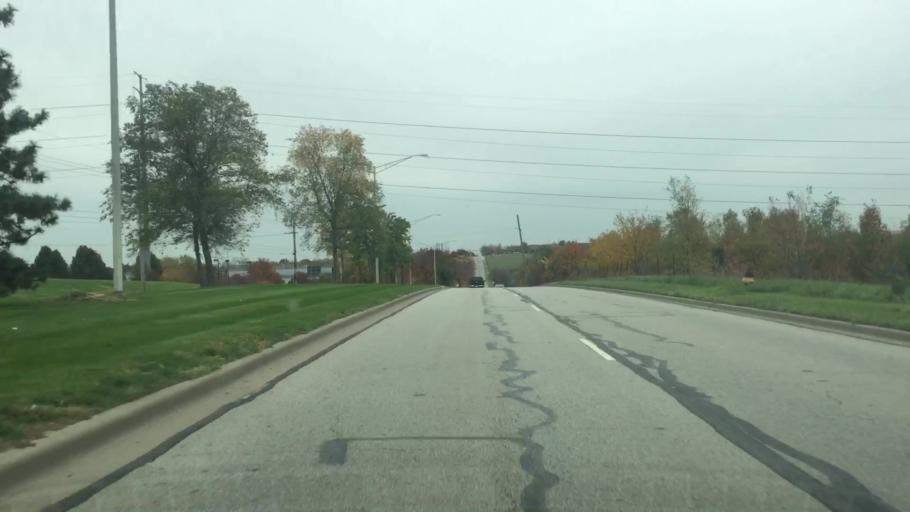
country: US
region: Kansas
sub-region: Johnson County
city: Lenexa
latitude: 38.9359
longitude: -94.7796
